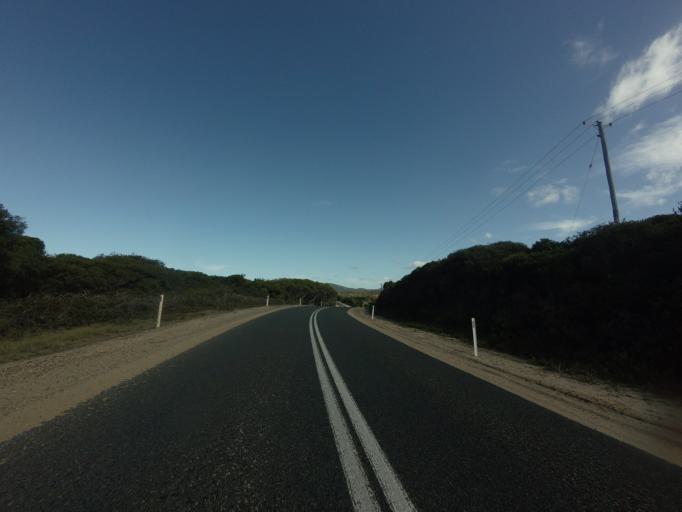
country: AU
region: Tasmania
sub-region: Break O'Day
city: St Helens
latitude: -41.8087
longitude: 148.2630
